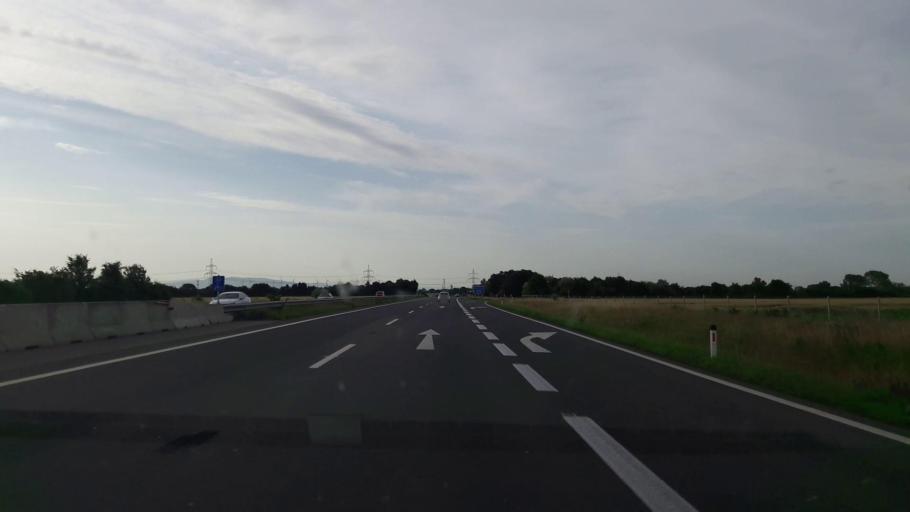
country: AT
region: Burgenland
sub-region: Eisenstadt-Umgebung
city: Steinbrunn
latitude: 47.8620
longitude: 16.4211
